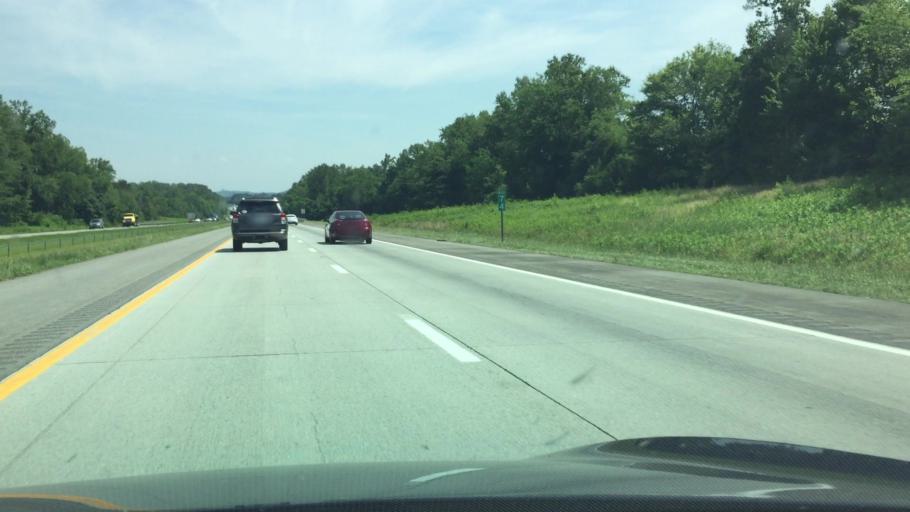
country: US
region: North Carolina
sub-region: Yadkin County
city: Jonesville
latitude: 36.1287
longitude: -80.8120
